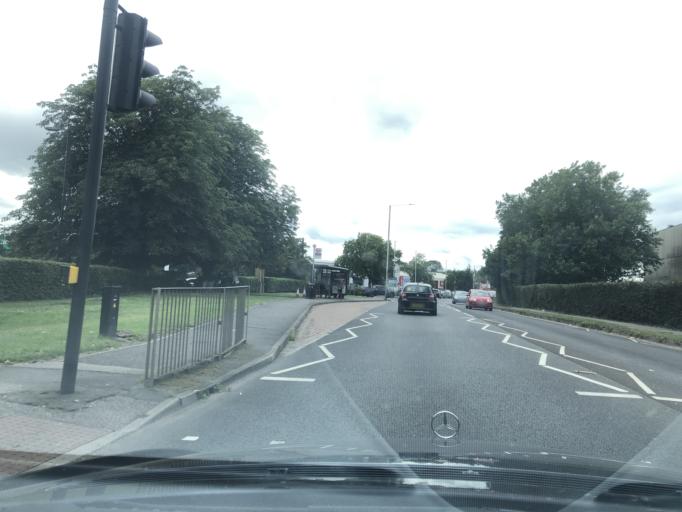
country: GB
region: England
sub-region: Greater London
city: Northolt
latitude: 51.5569
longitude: -0.3888
